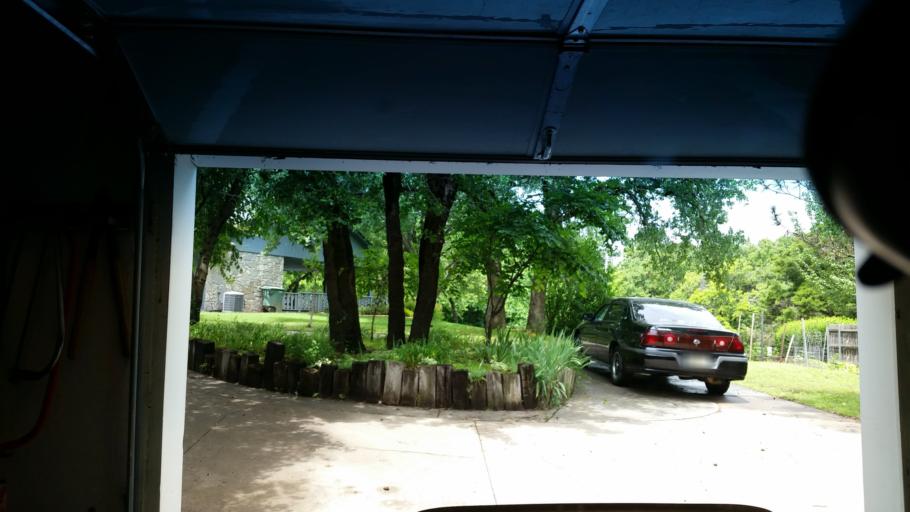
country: US
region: Oklahoma
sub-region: Oklahoma County
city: Edmond
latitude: 35.6414
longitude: -97.4331
